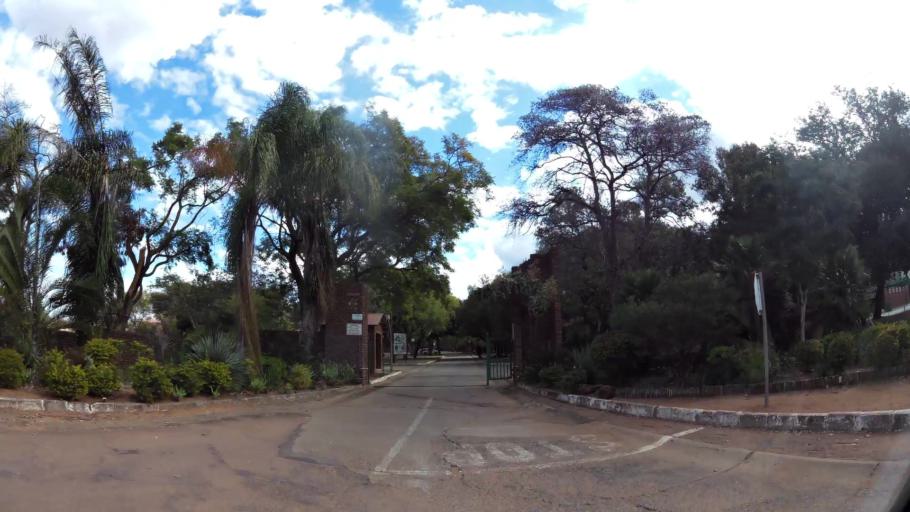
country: ZA
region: Limpopo
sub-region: Waterberg District Municipality
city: Modimolle
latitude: -24.7077
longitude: 28.3994
